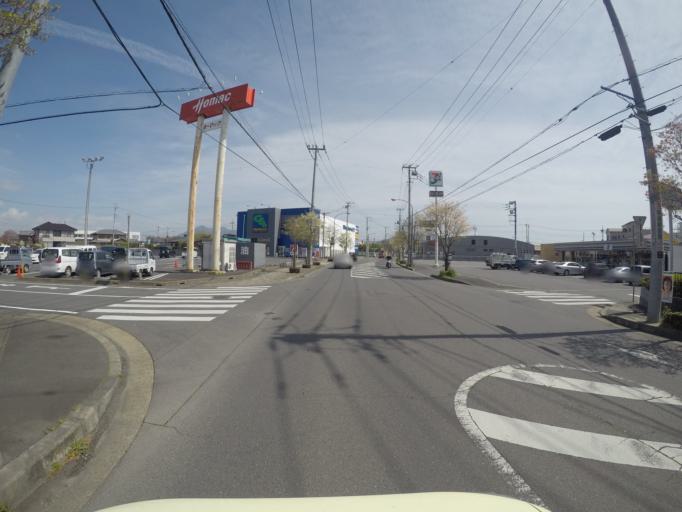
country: JP
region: Ibaraki
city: Tsukuba
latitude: 36.1345
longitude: 140.0815
